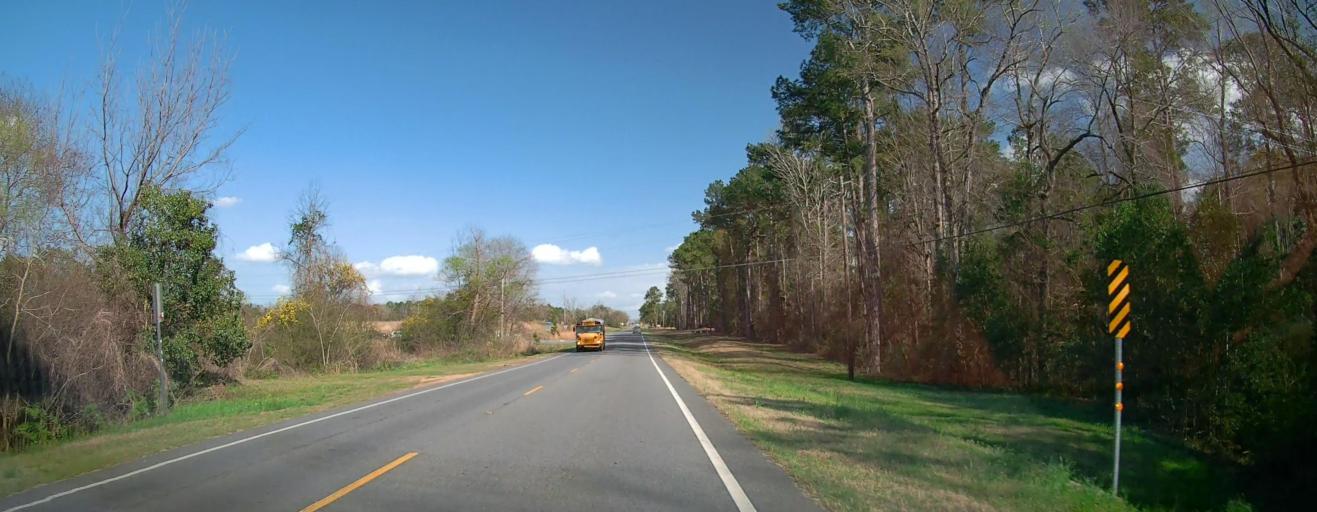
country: US
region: Georgia
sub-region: Dodge County
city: Eastman
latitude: 32.1966
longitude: -83.1962
